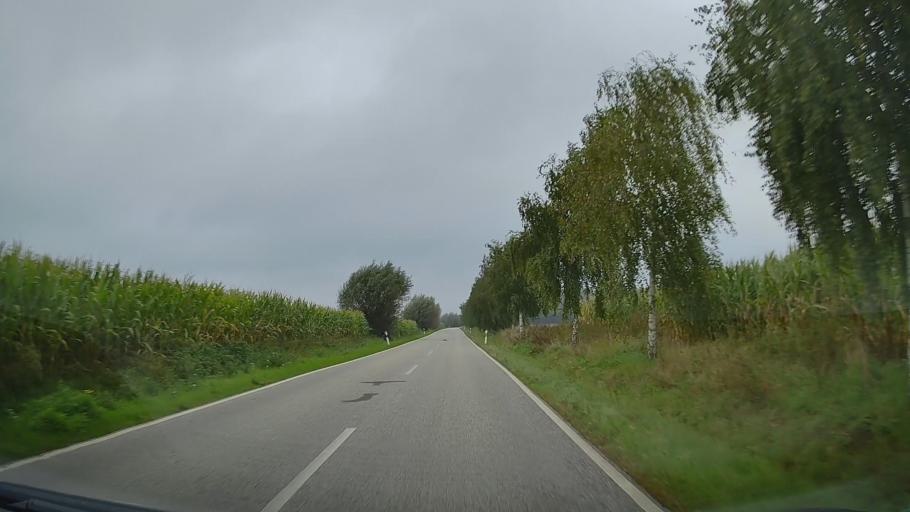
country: DE
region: Mecklenburg-Vorpommern
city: Blowatz
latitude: 53.9592
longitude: 11.5558
